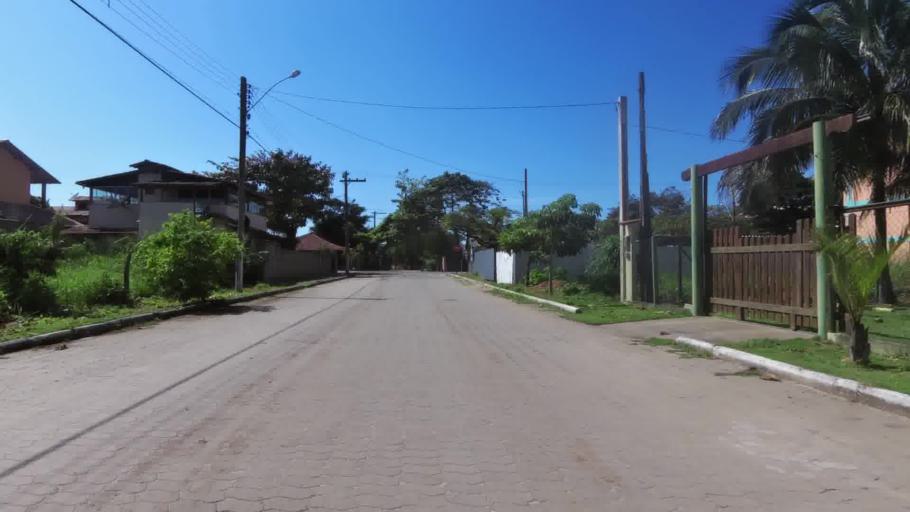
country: BR
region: Espirito Santo
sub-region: Piuma
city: Piuma
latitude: -20.8329
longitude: -40.6238
